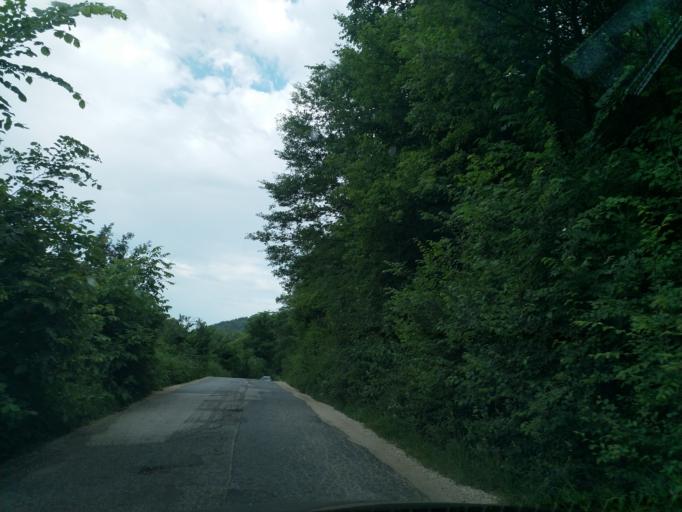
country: RS
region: Central Serbia
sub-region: Borski Okrug
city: Bor
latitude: 44.0235
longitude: 21.9781
